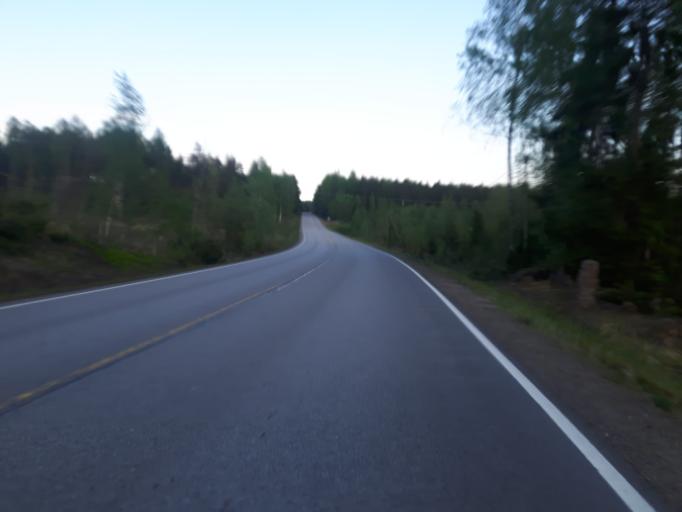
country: FI
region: Uusimaa
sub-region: Loviisa
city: Perna
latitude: 60.4557
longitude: 26.0852
